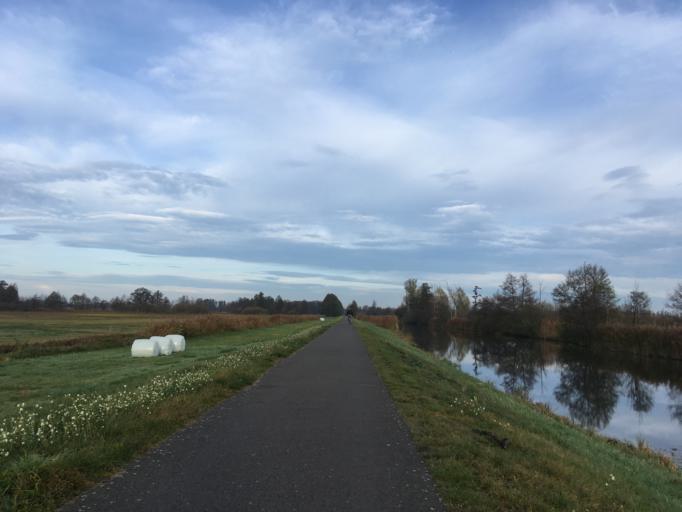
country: DE
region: Brandenburg
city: Luebben
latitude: 51.9101
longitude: 13.9231
